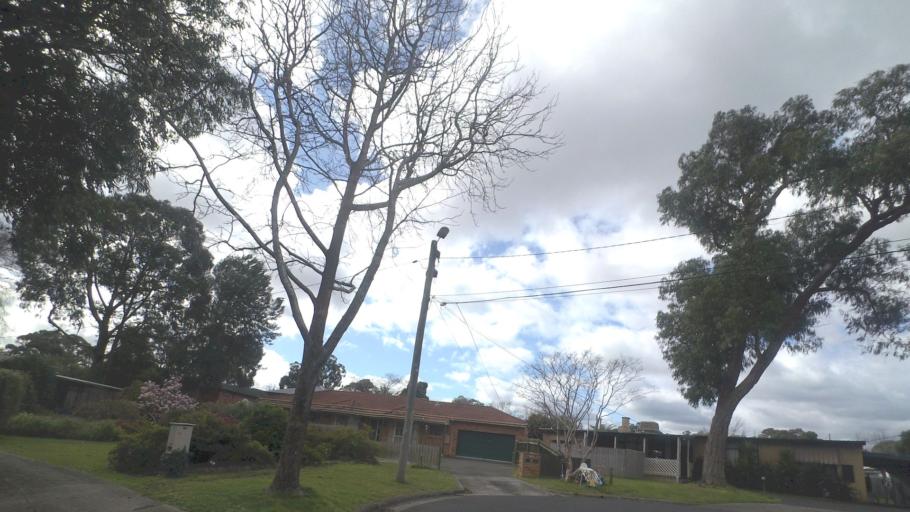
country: AU
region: Victoria
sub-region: Maroondah
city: Heathmont
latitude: -37.8272
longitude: 145.2336
